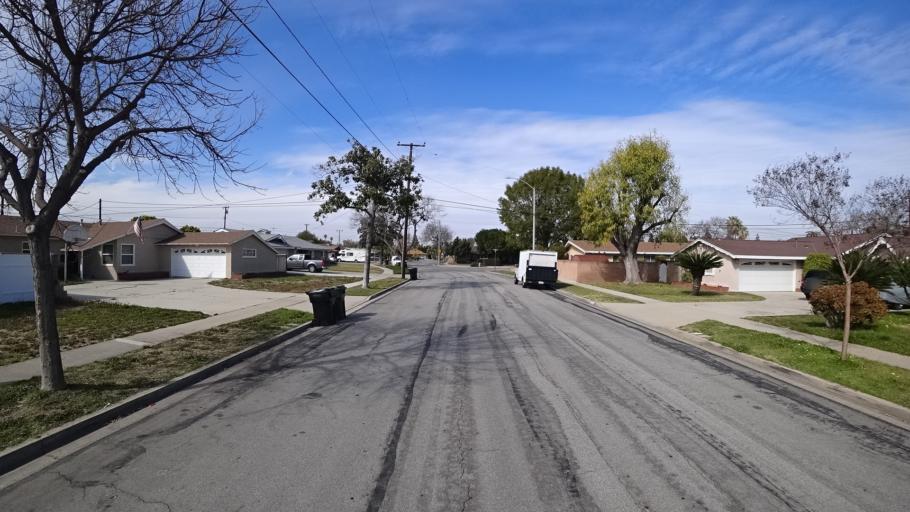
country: US
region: California
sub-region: Orange County
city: Anaheim
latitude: 33.7941
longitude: -117.9026
